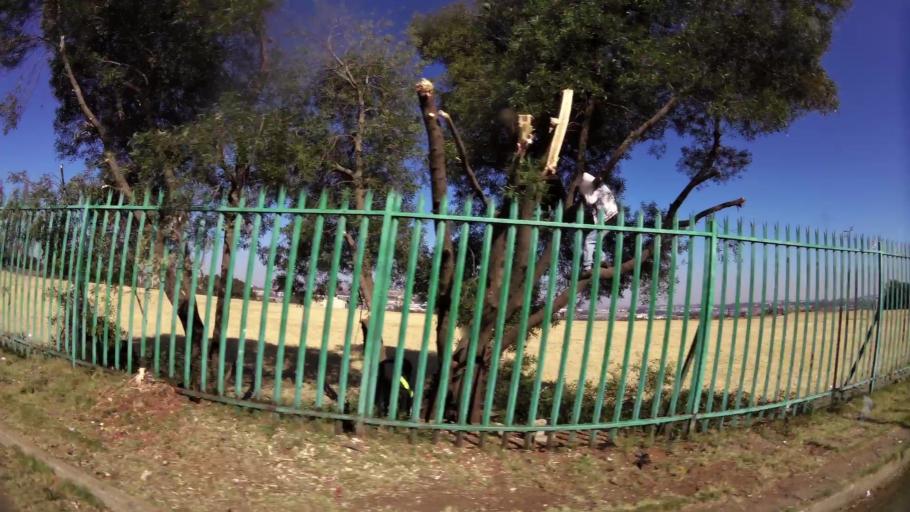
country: ZA
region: Gauteng
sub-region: City of Johannesburg Metropolitan Municipality
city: Johannesburg
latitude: -26.1924
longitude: 27.9753
